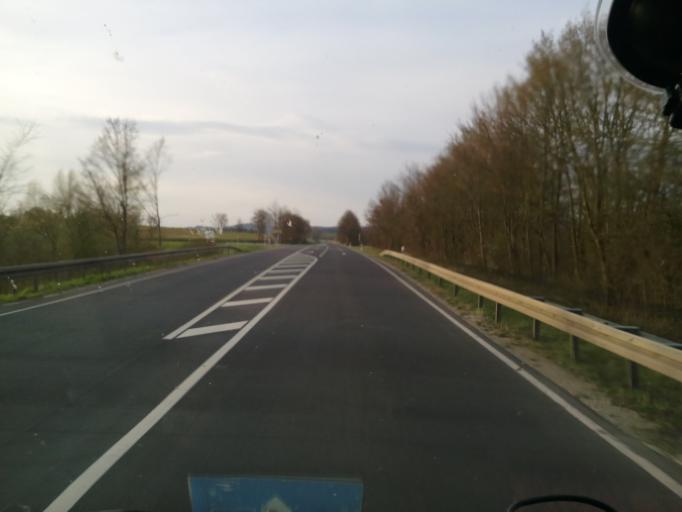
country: DE
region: Bavaria
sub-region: Regierungsbezirk Unterfranken
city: Pfarrweisach
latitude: 50.1244
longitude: 10.7614
